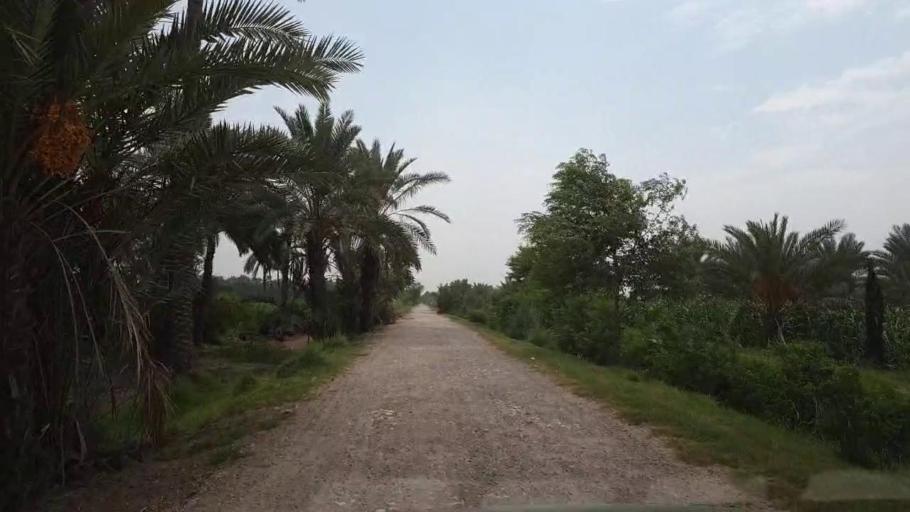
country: PK
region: Sindh
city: Pir jo Goth
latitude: 27.4951
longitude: 68.5996
